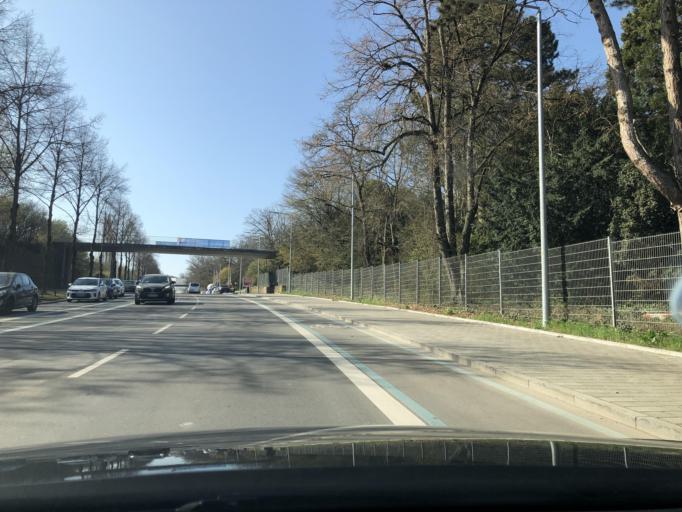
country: FR
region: Haute-Normandie
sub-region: Departement de la Seine-Maritime
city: Jumieges
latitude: 49.4167
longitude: 0.8339
